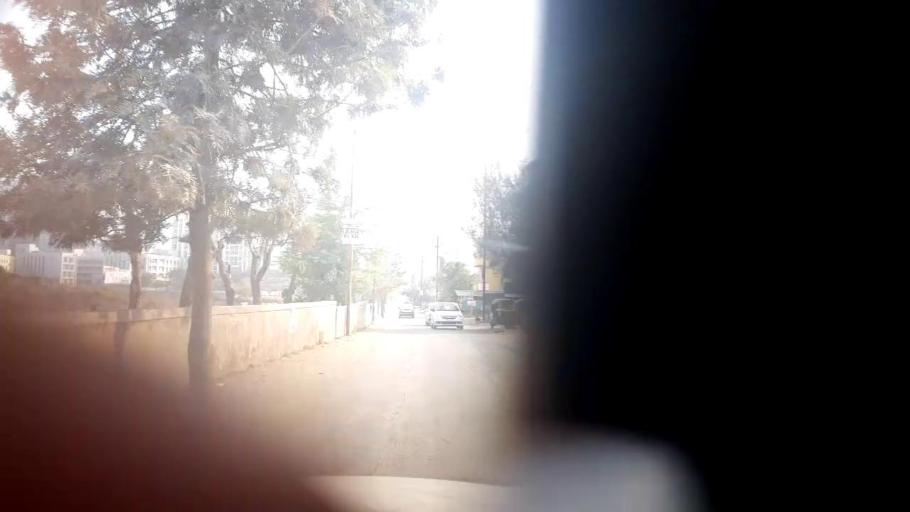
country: IN
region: Maharashtra
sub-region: Pune Division
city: Pimpri
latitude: 18.5768
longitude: 73.7707
